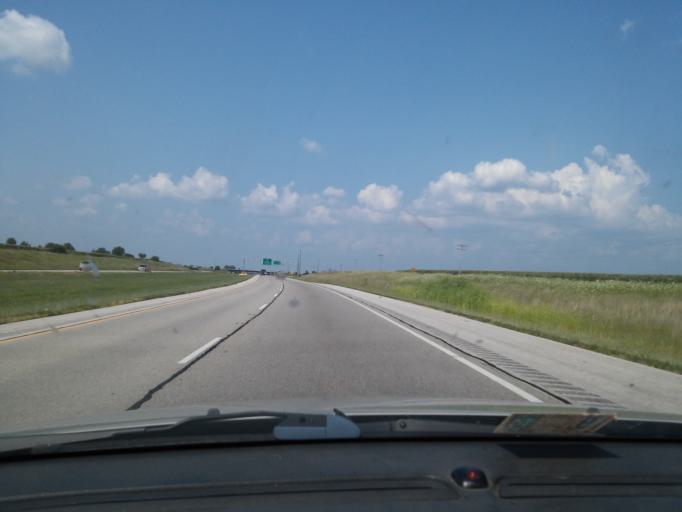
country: US
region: Illinois
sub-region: McLean County
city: Twin Grove
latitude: 40.4011
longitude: -89.0582
